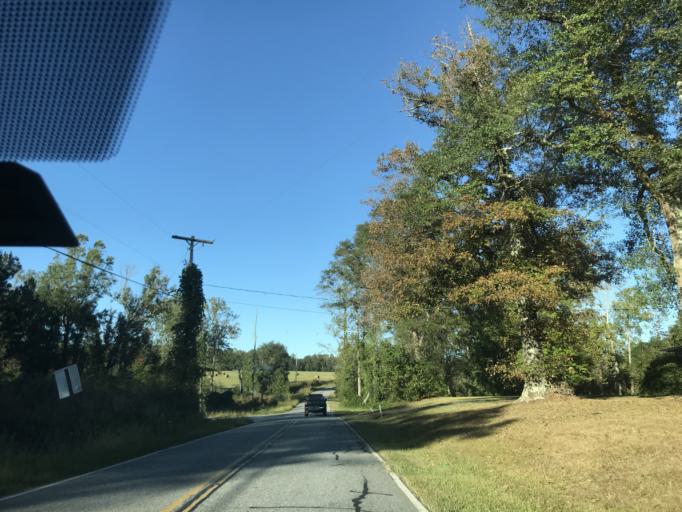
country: US
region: South Carolina
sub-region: Spartanburg County
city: Mayo
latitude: 35.1021
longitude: -81.8476
